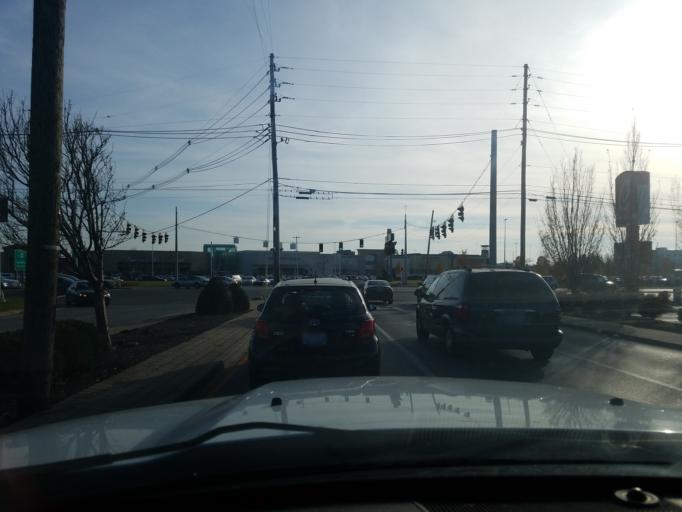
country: US
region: Kentucky
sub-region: Jefferson County
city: Beechwood Village
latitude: 38.2508
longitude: -85.6236
